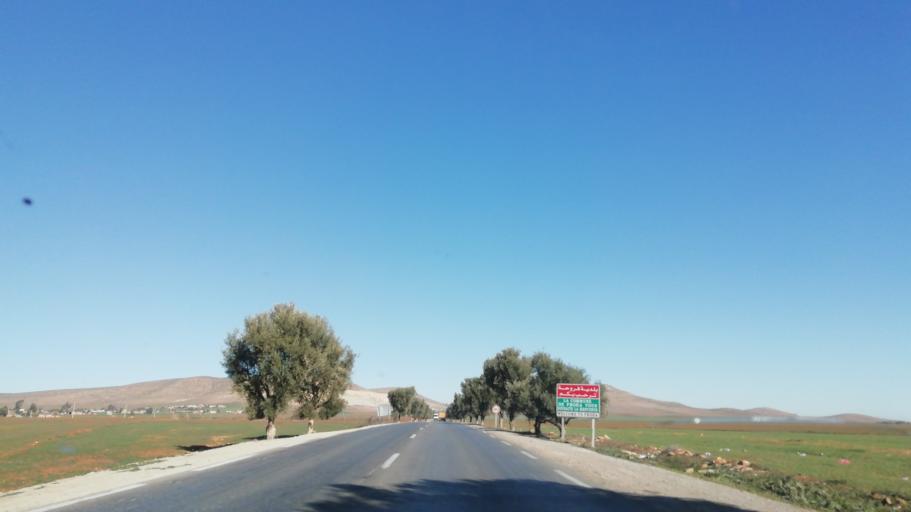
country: DZ
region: Mascara
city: Mascara
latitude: 35.2188
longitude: 0.1127
